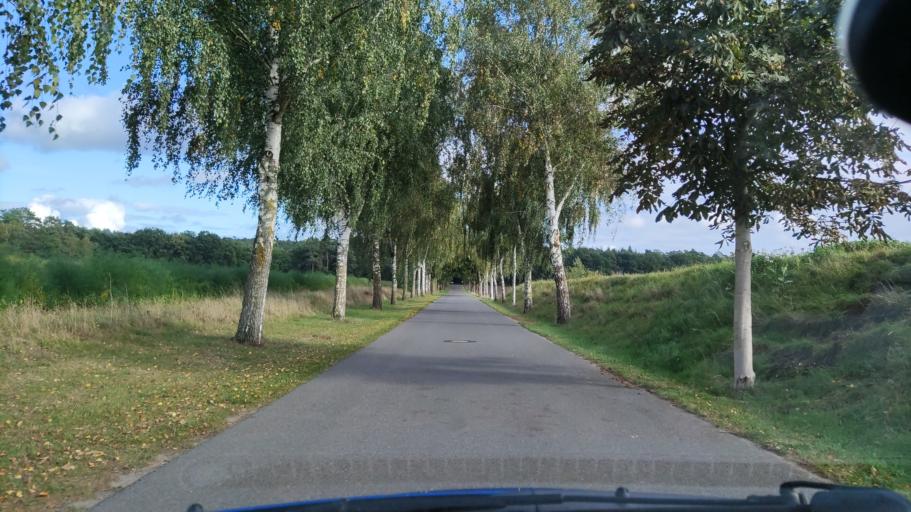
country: DE
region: Lower Saxony
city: Deutsch Evern
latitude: 53.2004
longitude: 10.4458
